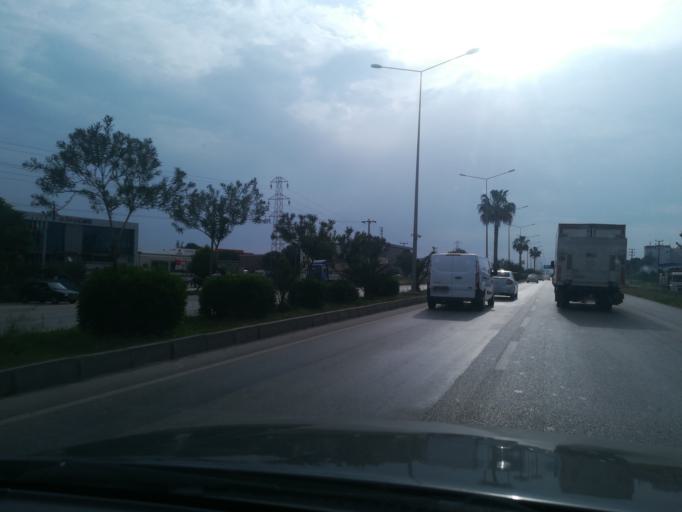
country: TR
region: Adana
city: Yuregir
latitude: 36.9841
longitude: 35.3872
